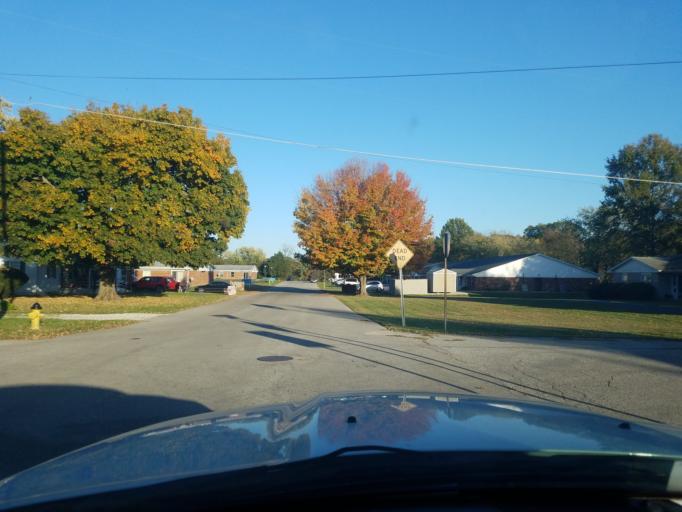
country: US
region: Indiana
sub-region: Washington County
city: Salem
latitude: 38.5956
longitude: -86.0956
